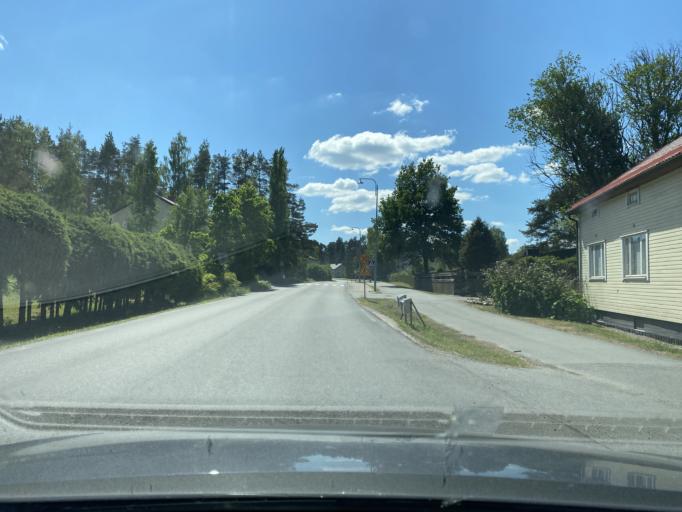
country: FI
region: Satakunta
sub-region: Rauma
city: Eura
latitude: 61.1231
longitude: 22.1602
